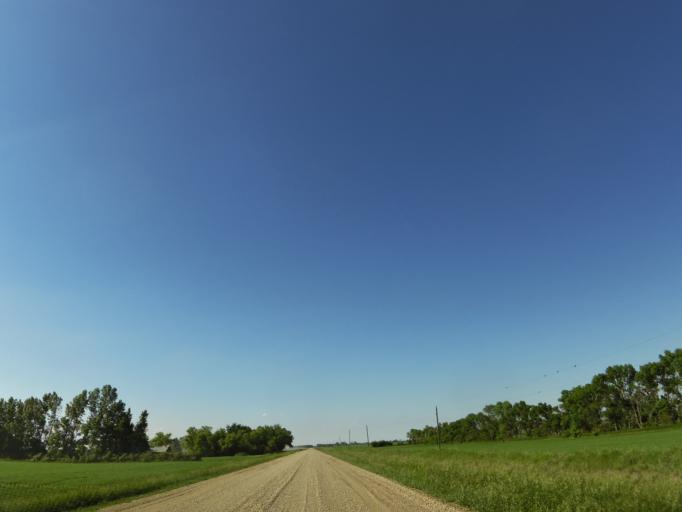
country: US
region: North Dakota
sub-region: Walsh County
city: Grafton
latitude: 48.3572
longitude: -97.2559
